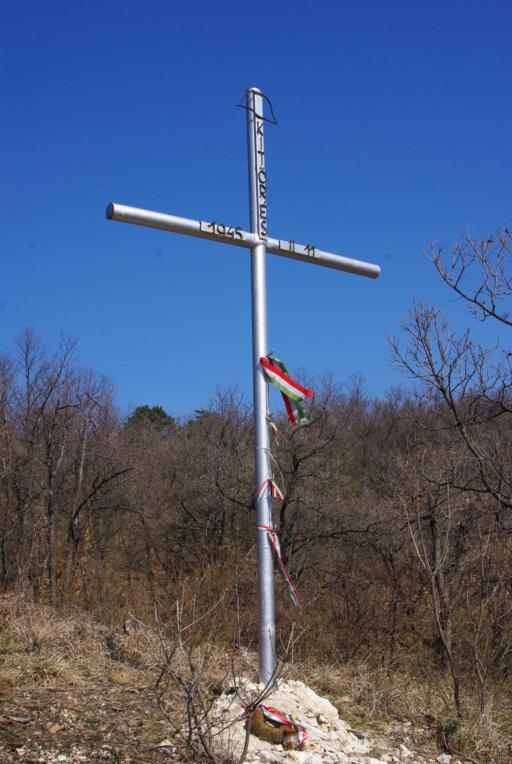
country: HU
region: Pest
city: Telki
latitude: 47.5427
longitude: 18.8703
